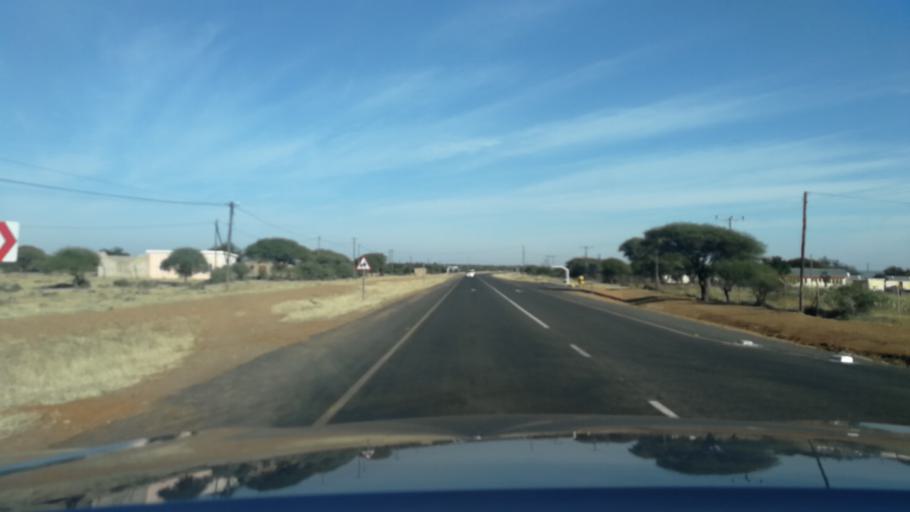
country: BW
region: South East
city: Janeng
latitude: -25.4687
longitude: 25.5678
